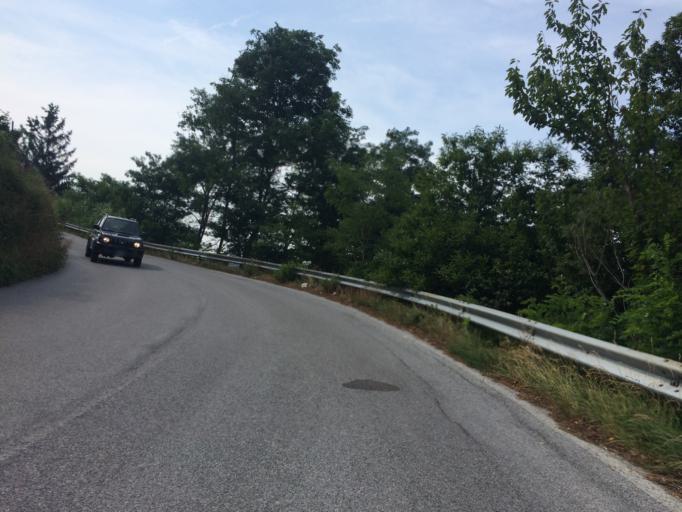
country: IT
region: Liguria
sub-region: Provincia di Savona
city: San Giovanni
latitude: 44.4030
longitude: 8.4894
